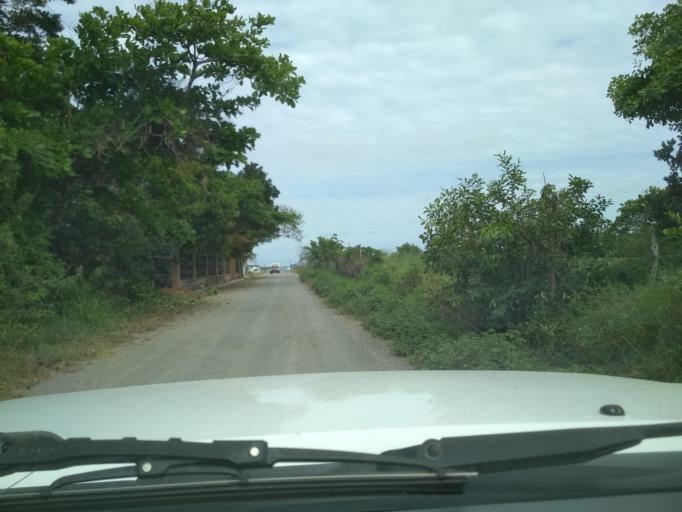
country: MX
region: Veracruz
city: Anton Lizardo
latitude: 19.0314
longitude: -95.9697
